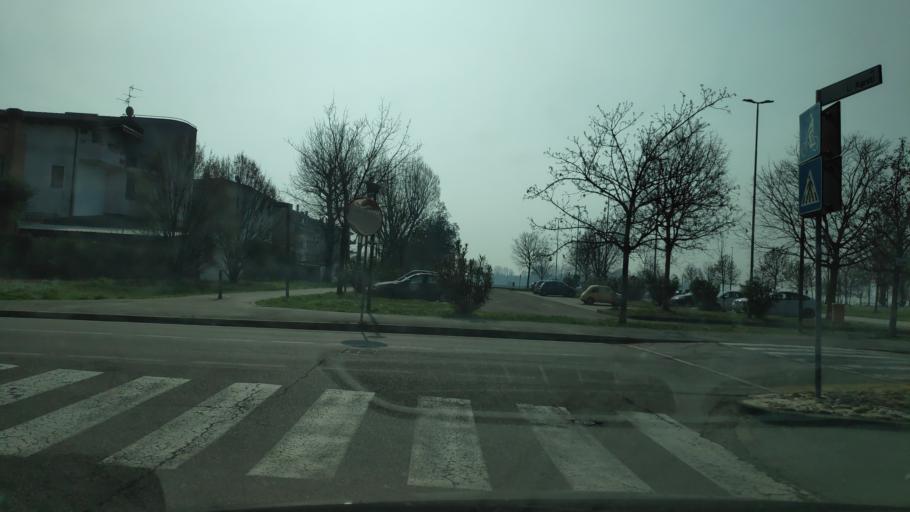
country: IT
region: Lombardy
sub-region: Citta metropolitana di Milano
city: Liscate
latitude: 45.4806
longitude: 9.4049
